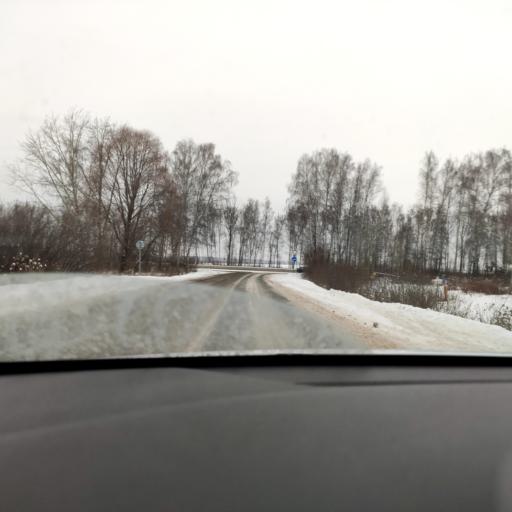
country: RU
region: Tatarstan
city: Osinovo
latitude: 55.8605
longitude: 48.8205
